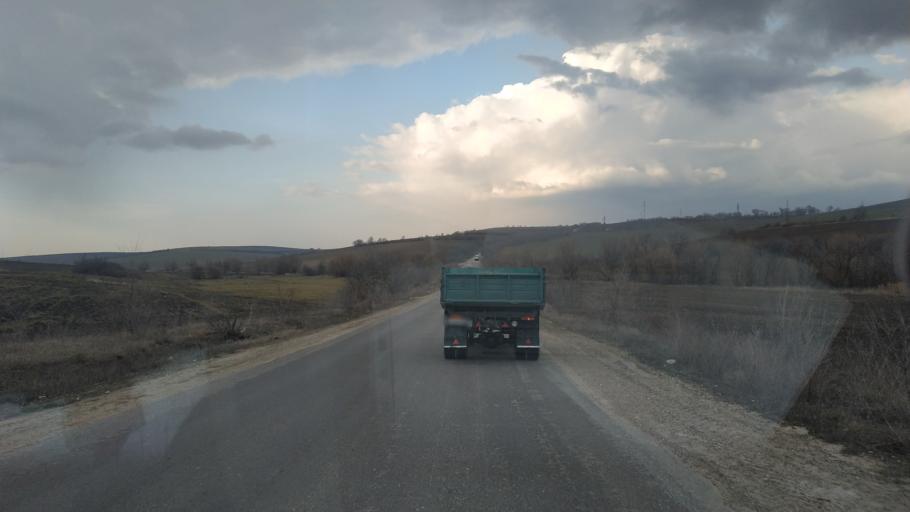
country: MD
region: Anenii Noi
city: Anenii Noi
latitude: 46.9455
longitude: 29.2831
